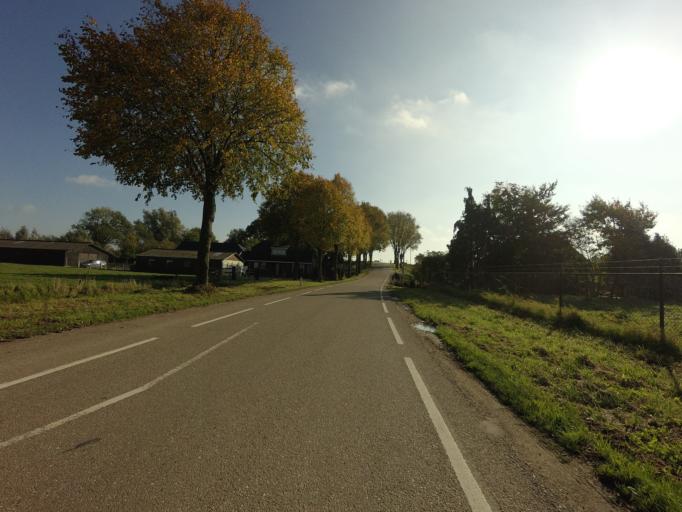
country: NL
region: Gelderland
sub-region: Gemeente Culemborg
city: Culemborg
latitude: 51.9557
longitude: 5.1674
